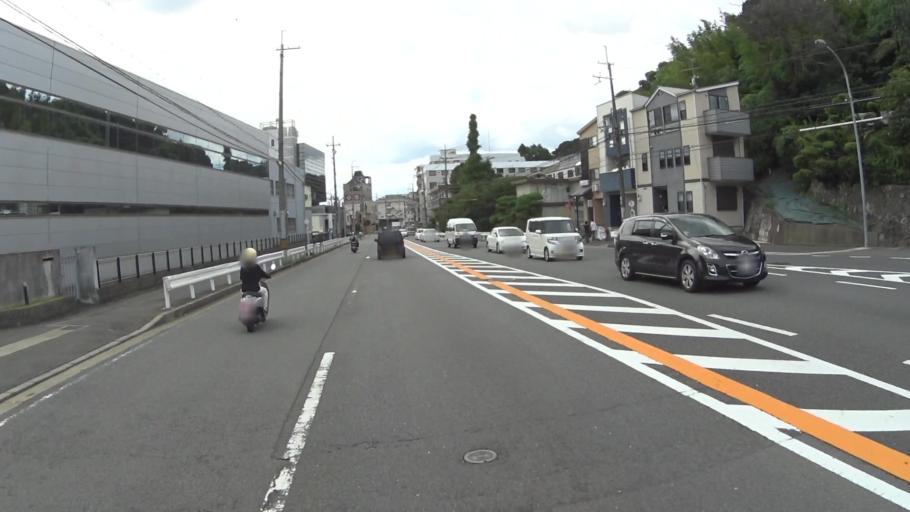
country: JP
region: Kyoto
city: Uji
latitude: 34.9313
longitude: 135.7830
